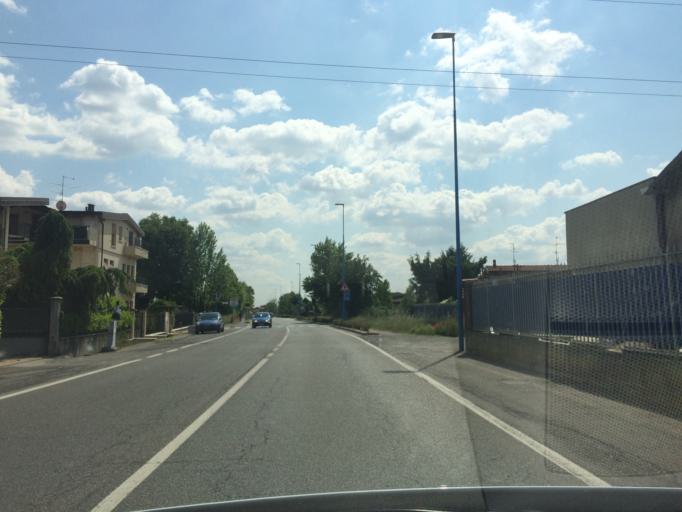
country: IT
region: Lombardy
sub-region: Provincia di Brescia
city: Folzano
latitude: 45.5136
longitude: 10.1940
